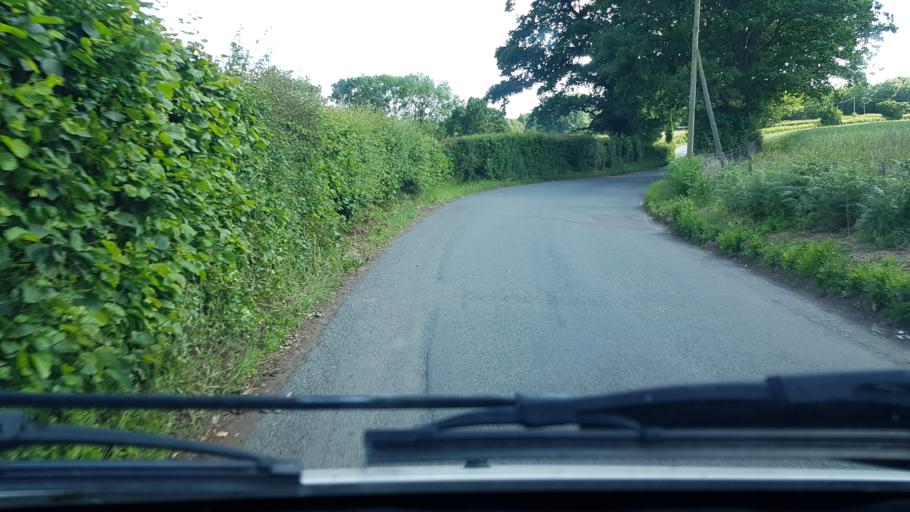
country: GB
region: England
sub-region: Worcestershire
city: Bewdley
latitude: 52.4109
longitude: -2.3071
